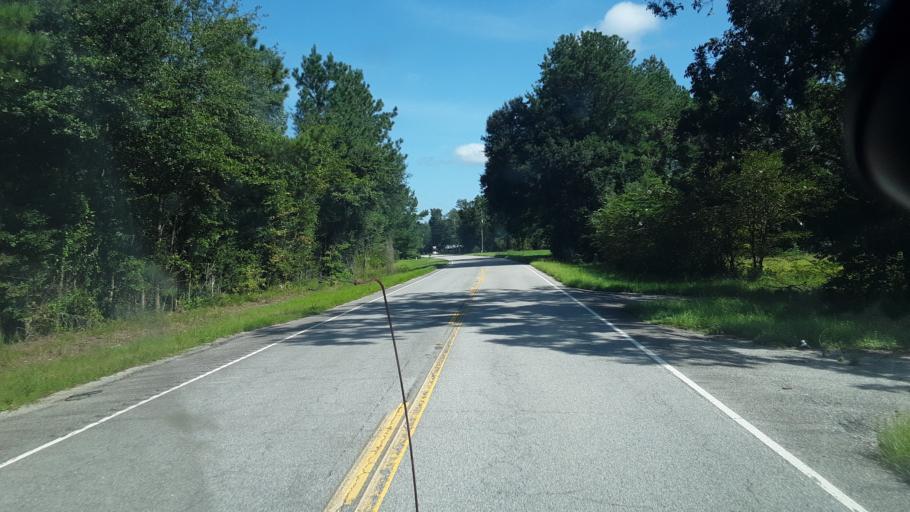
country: US
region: South Carolina
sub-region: Hampton County
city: Varnville
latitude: 32.7717
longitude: -81.0511
